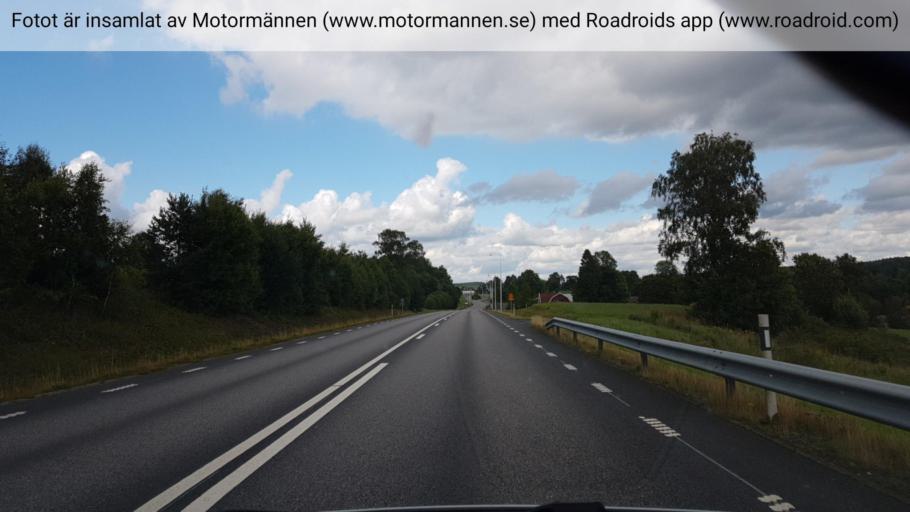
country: SE
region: Vaestra Goetaland
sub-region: Ulricehamns Kommun
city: Ulricehamn
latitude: 57.9153
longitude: 13.4845
